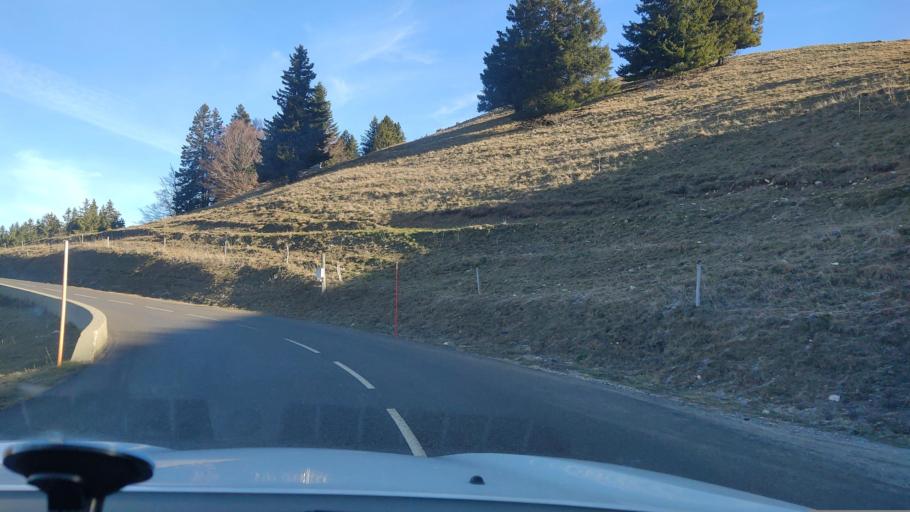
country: FR
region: Rhone-Alpes
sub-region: Departement de la Savoie
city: Mouxy
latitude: 45.6734
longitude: 5.9750
